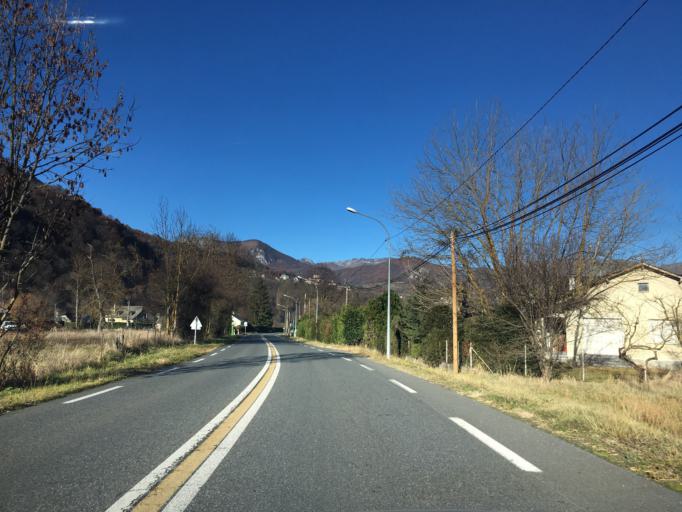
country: FR
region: Midi-Pyrenees
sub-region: Departement des Hautes-Pyrenees
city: Pierrefitte-Nestalas
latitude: 42.9744
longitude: -0.0769
